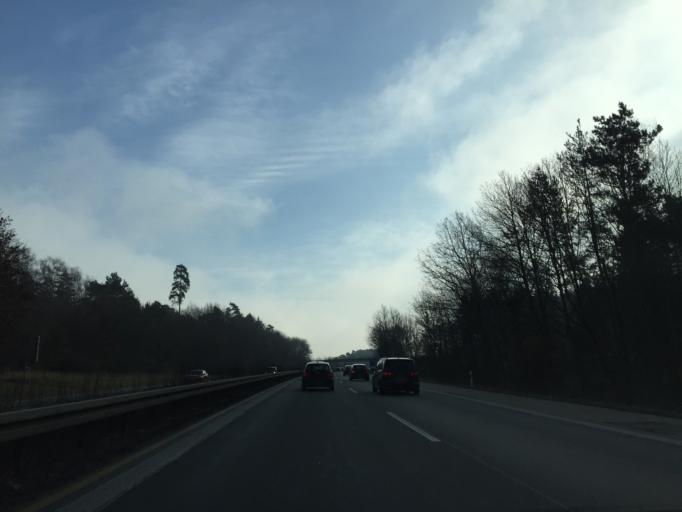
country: DE
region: Bavaria
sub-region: Regierungsbezirk Unterfranken
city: Geiselwind
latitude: 49.7857
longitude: 10.4263
